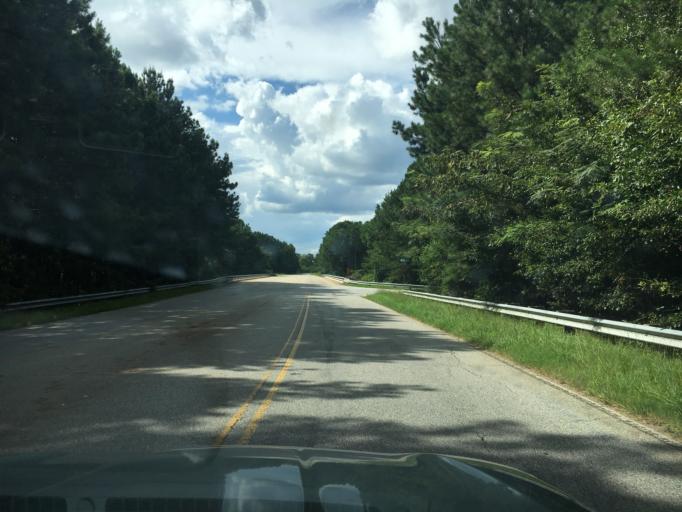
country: US
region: South Carolina
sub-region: Spartanburg County
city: Southern Shops
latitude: 34.9990
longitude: -81.9887
